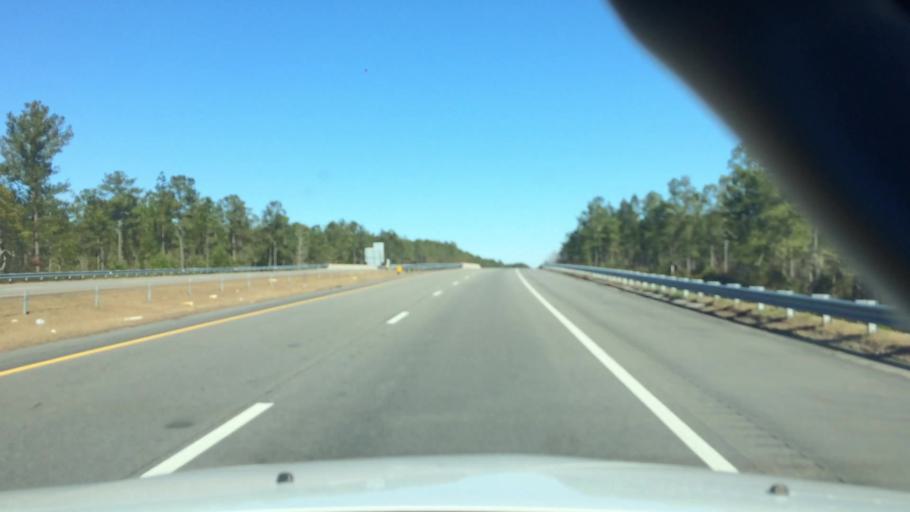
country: US
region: North Carolina
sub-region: Brunswick County
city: Leland
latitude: 34.2172
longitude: -78.0768
